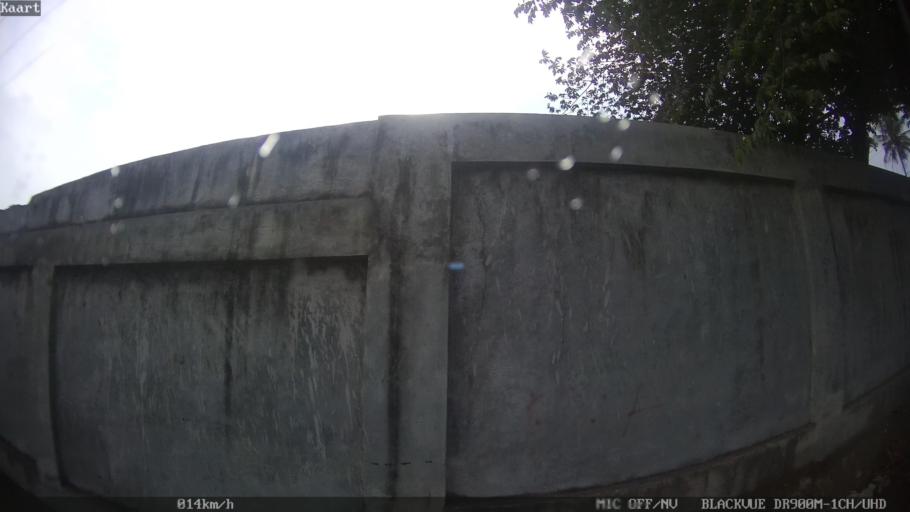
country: ID
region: Lampung
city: Bandarlampung
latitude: -5.4126
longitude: 105.2939
